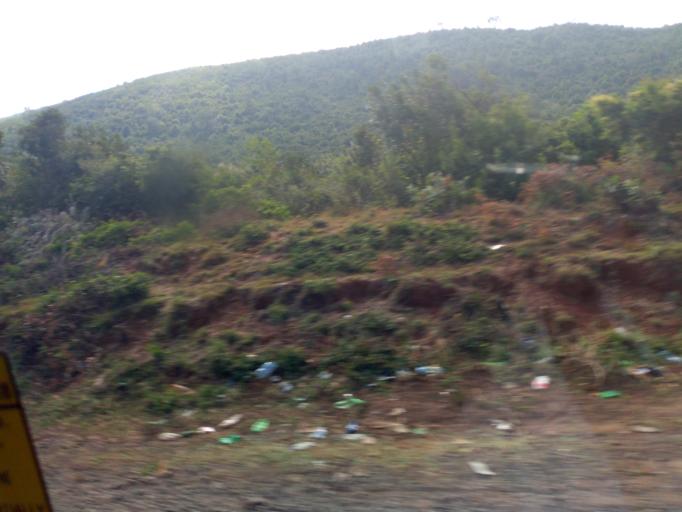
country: KE
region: Nakuru
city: Kijabe
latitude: -1.0165
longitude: 36.6010
